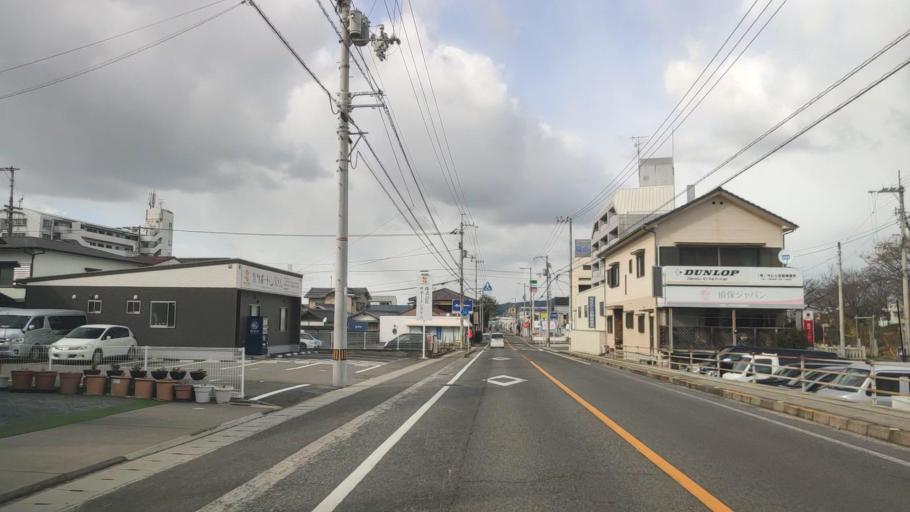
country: JP
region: Ehime
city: Saijo
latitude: 34.0483
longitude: 133.0172
